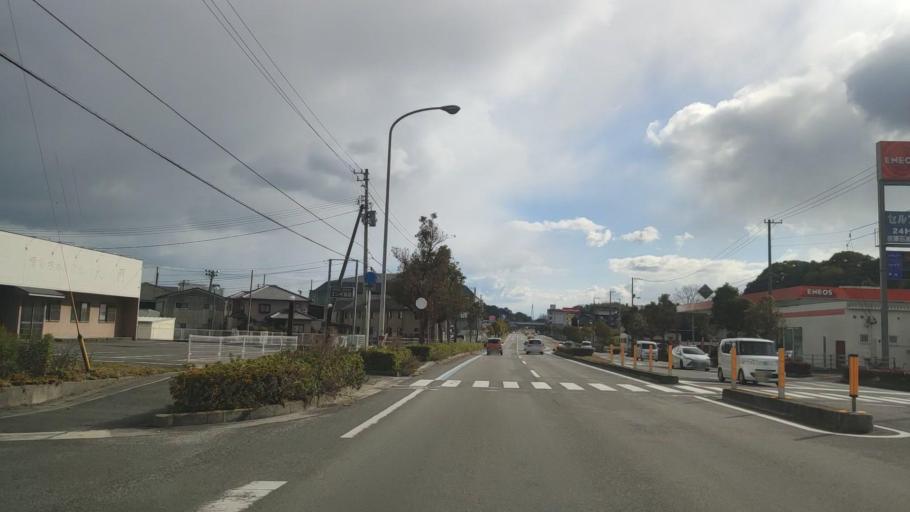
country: JP
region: Ehime
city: Hojo
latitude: 34.0605
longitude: 132.9657
